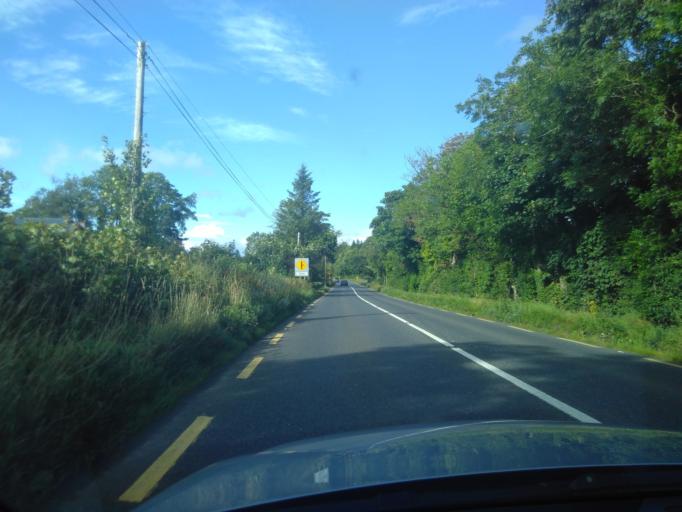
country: IE
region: Ulster
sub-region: County Donegal
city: Ballybofey
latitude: 54.8228
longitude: -7.7530
